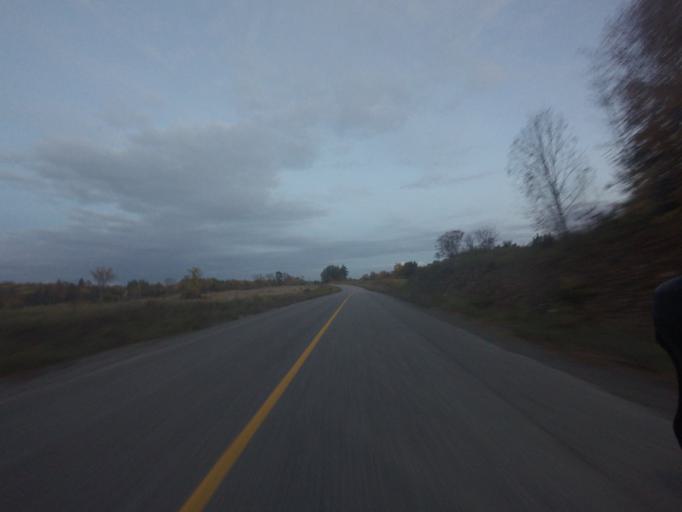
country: CA
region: Ontario
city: Renfrew
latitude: 45.3394
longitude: -76.9136
